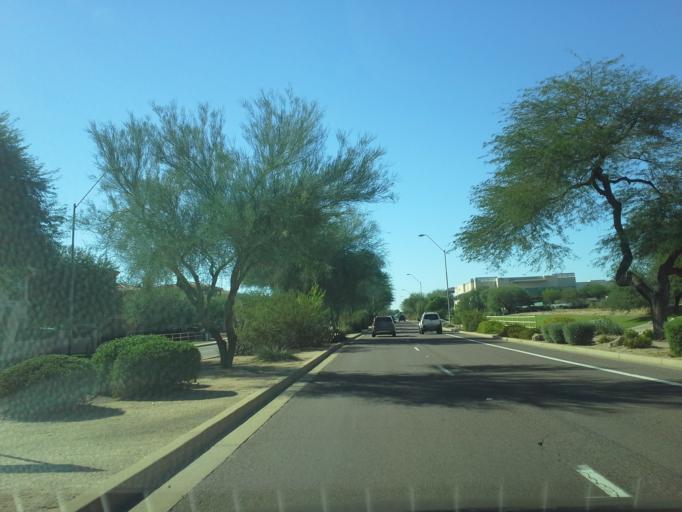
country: US
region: Arizona
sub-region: Maricopa County
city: Paradise Valley
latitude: 33.6401
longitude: -111.8986
